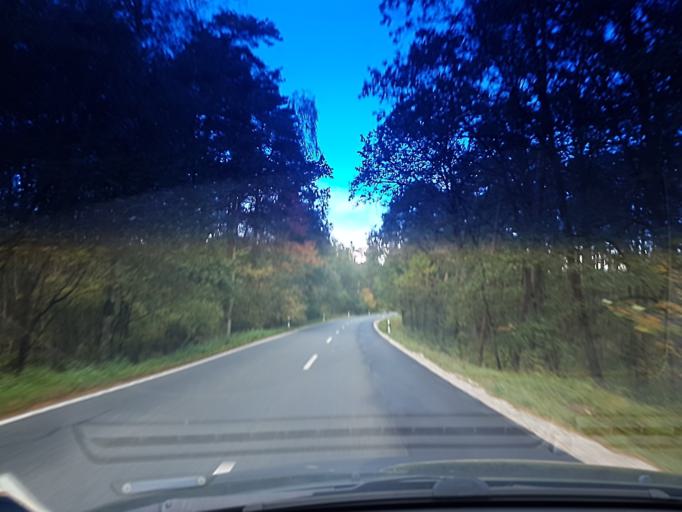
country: DE
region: Bavaria
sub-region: Regierungsbezirk Mittelfranken
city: Hochstadt an der Aisch
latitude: 49.7352
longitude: 10.8179
